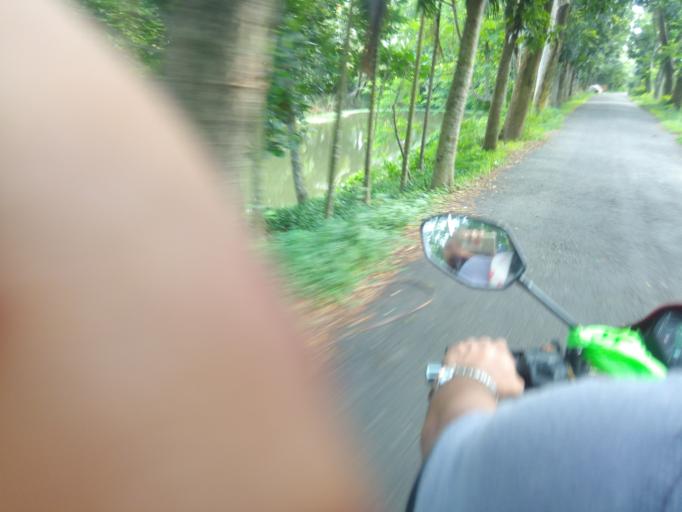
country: BD
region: Khulna
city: Kalia
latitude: 22.9583
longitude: 89.5542
